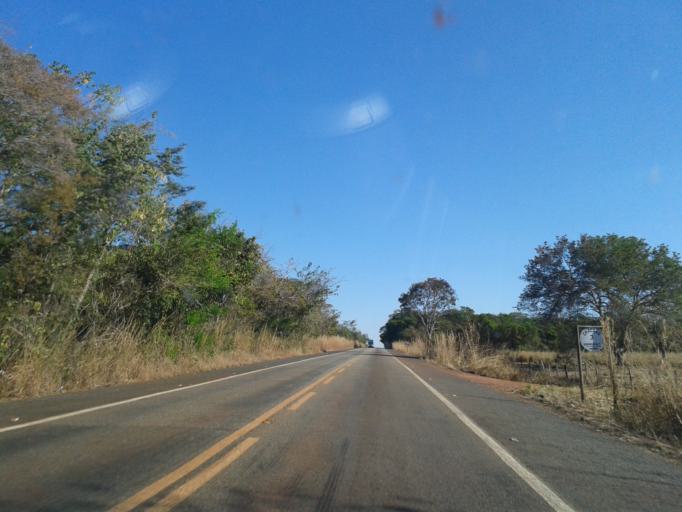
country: BR
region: Goias
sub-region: Mozarlandia
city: Mozarlandia
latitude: -15.0443
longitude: -50.6066
